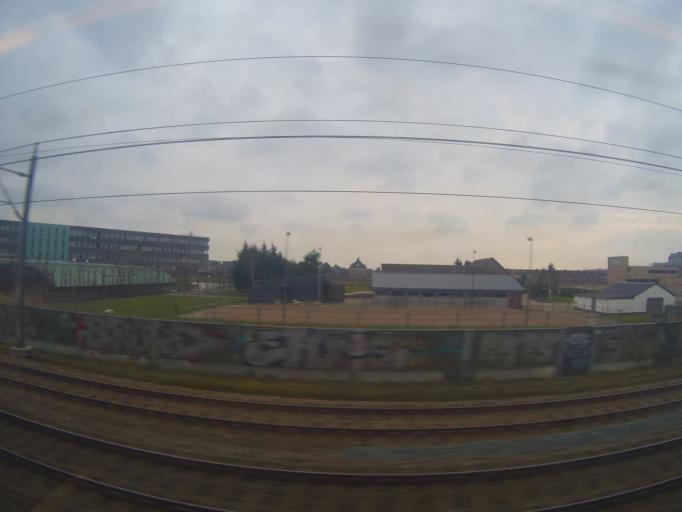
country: NL
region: Utrecht
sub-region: Gemeente Woerden
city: Woerden
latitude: 52.0896
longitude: 4.9072
